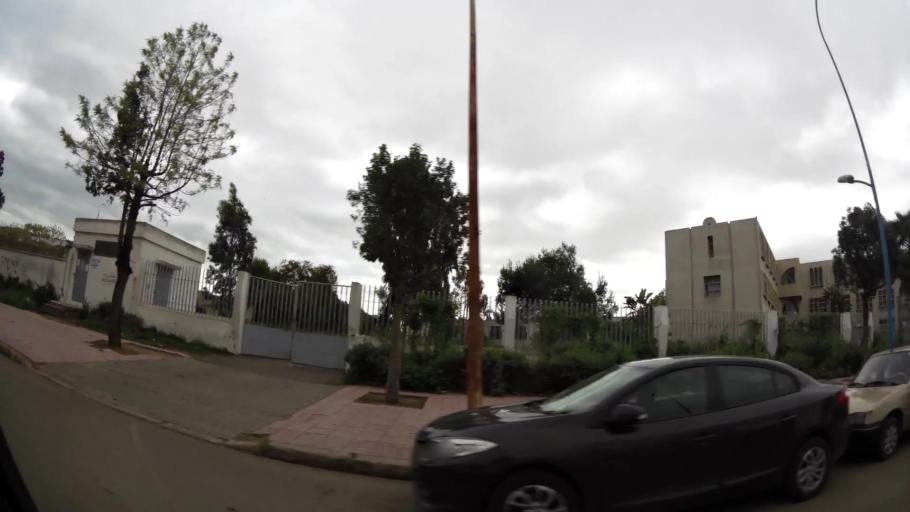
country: MA
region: Grand Casablanca
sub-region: Mediouna
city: Tit Mellil
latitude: 33.5644
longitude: -7.5306
